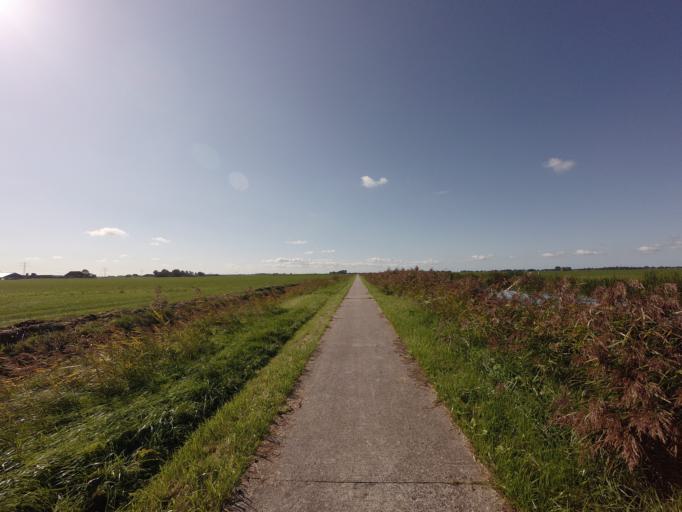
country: NL
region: Friesland
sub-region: Gemeente Boarnsterhim
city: Reduzum
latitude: 53.1389
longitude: 5.7618
